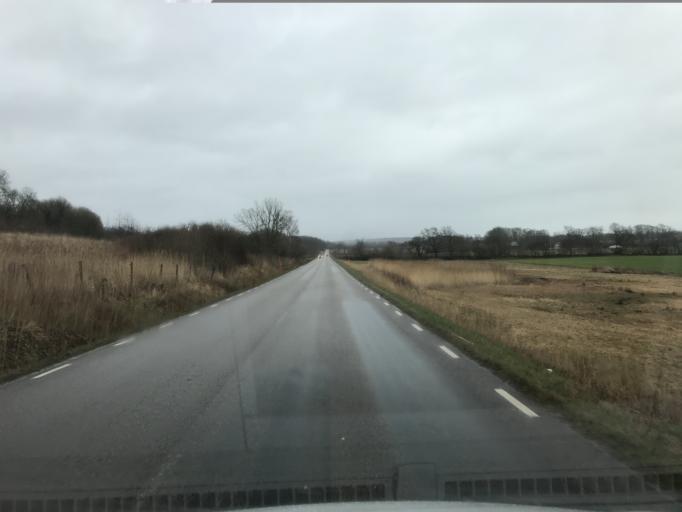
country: SE
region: Skane
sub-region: Bastads Kommun
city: Forslov
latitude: 56.3444
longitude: 12.8662
